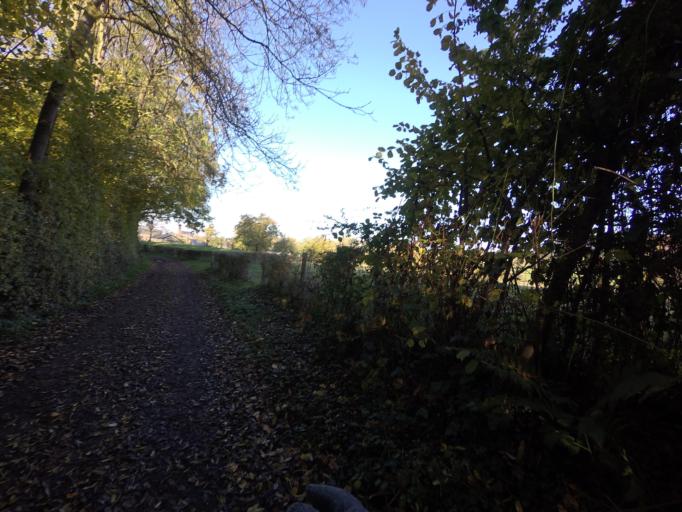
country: BE
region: Wallonia
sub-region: Province de Liege
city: Plombieres
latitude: 50.7798
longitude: 5.9599
